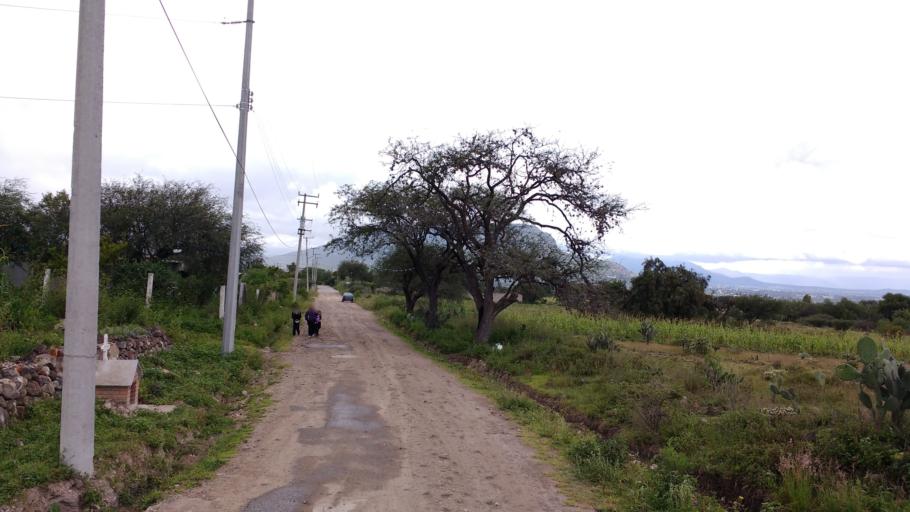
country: MX
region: Hidalgo
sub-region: Tezontepec de Aldama
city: Tenango
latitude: 20.2750
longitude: -99.2782
